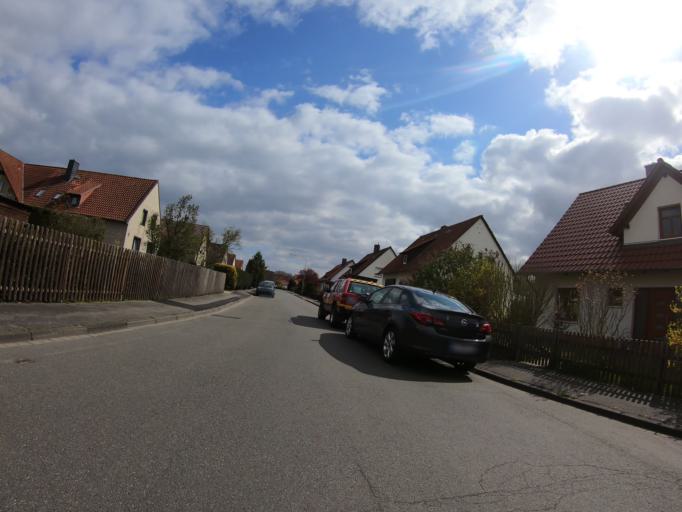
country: DE
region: Lower Saxony
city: Gifhorn
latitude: 52.4826
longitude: 10.5127
